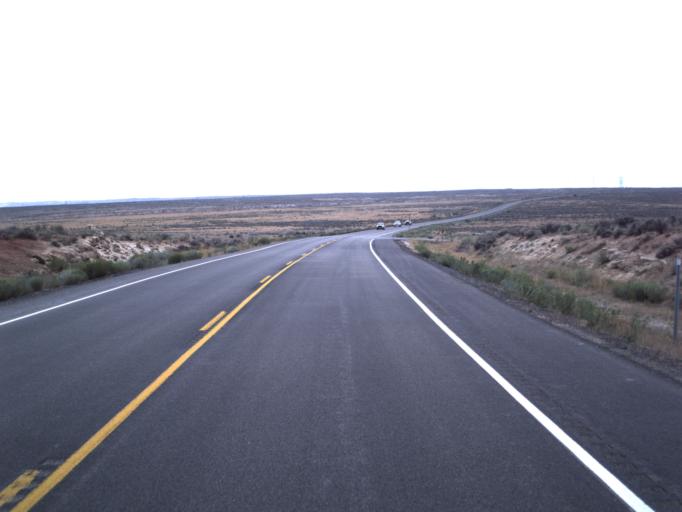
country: US
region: Utah
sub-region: Uintah County
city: Naples
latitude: 40.2499
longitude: -109.4248
